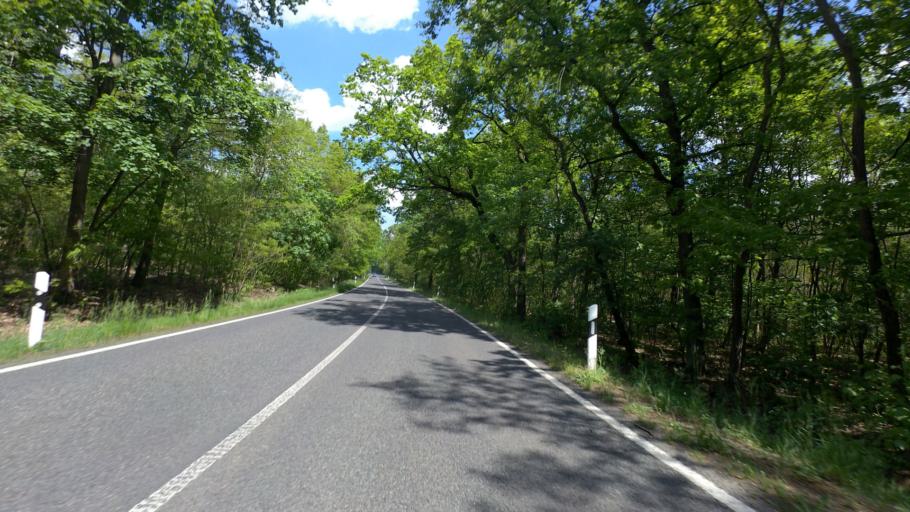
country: DE
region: Brandenburg
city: Straupitz
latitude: 51.9445
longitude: 14.1751
